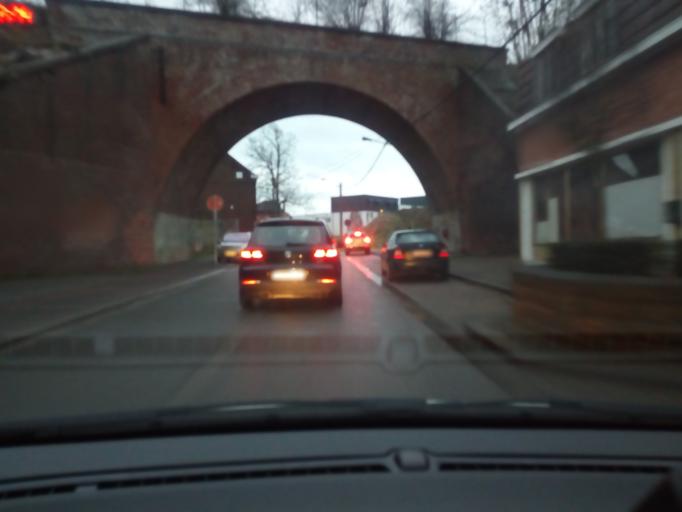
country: BE
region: Wallonia
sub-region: Province du Hainaut
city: Estinnes-au-Val
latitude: 50.4566
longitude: 4.0942
